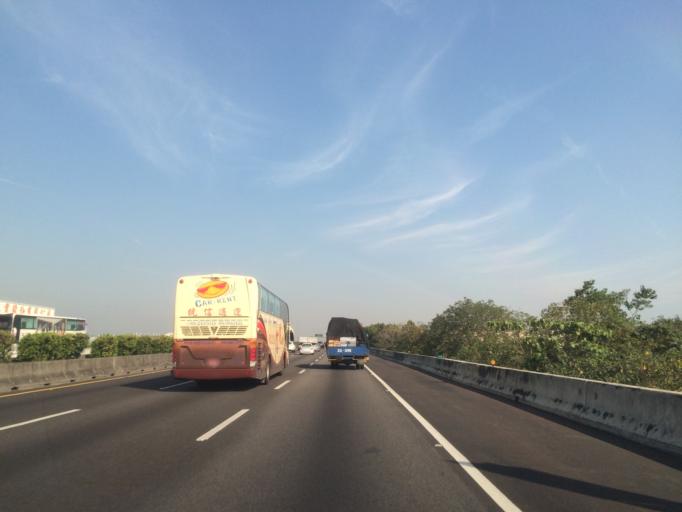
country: TW
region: Taiwan
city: Fengyuan
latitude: 24.2346
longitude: 120.6878
